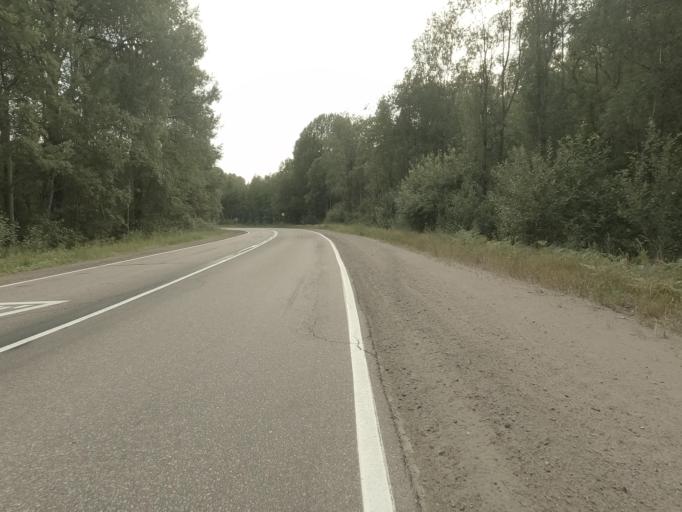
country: RU
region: Leningrad
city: Kamennogorsk
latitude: 60.8704
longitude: 28.9809
